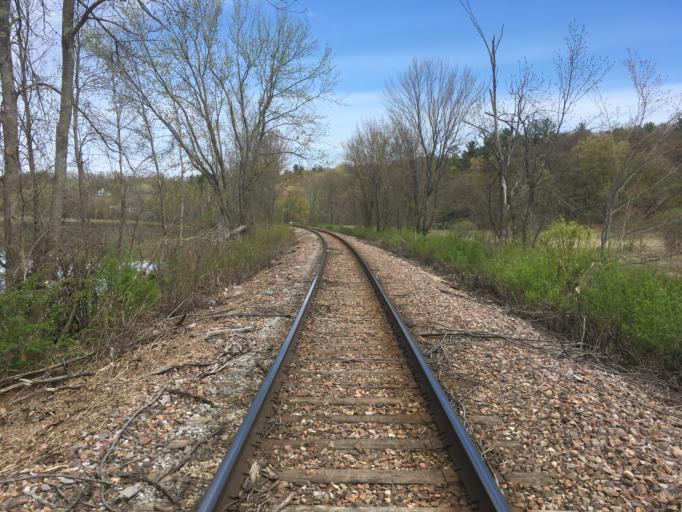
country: US
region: Vermont
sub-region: Rutland County
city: Brandon
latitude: 43.7060
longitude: -73.0363
